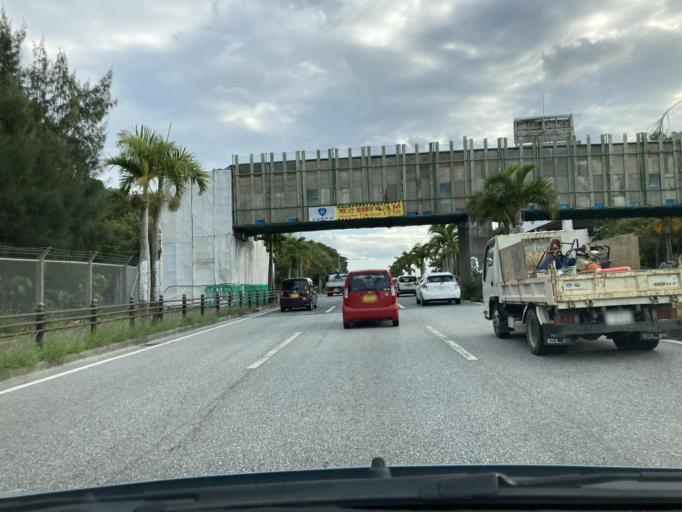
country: JP
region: Okinawa
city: Chatan
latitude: 26.3365
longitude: 127.7515
